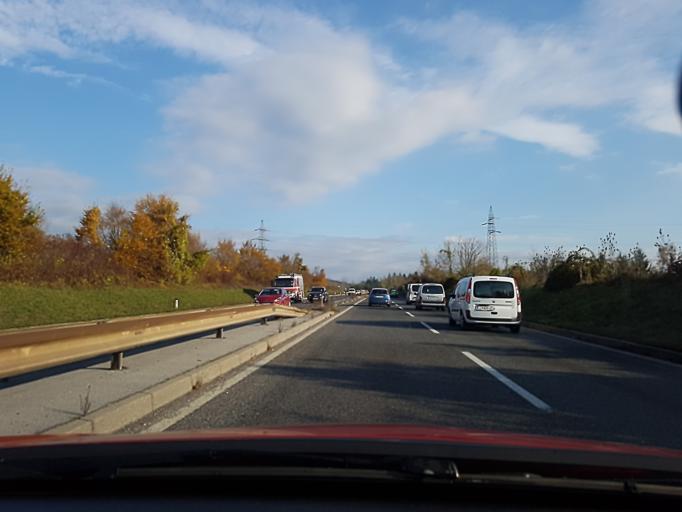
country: SI
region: Ljubljana
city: Ljubljana
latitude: 46.0845
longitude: 14.5304
